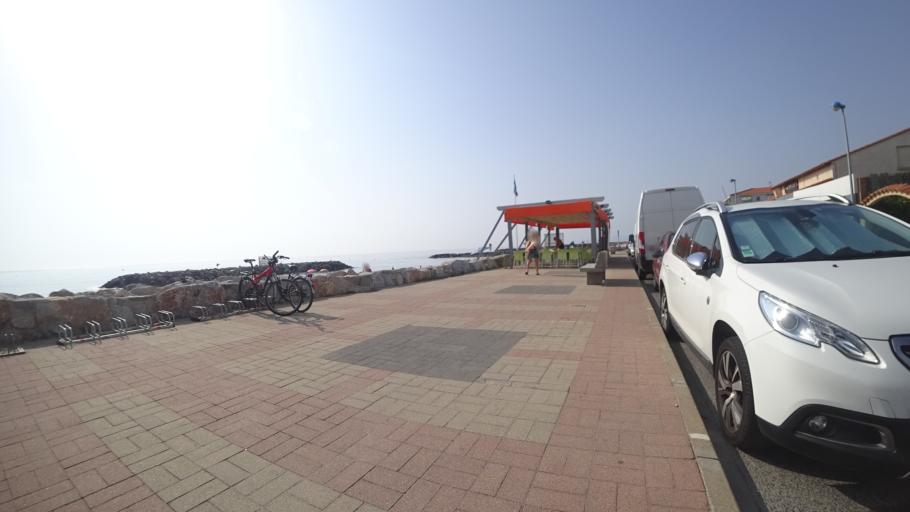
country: FR
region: Languedoc-Roussillon
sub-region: Departement des Pyrenees-Orientales
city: Sainte-Marie-Plage
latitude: 42.7259
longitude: 3.0389
